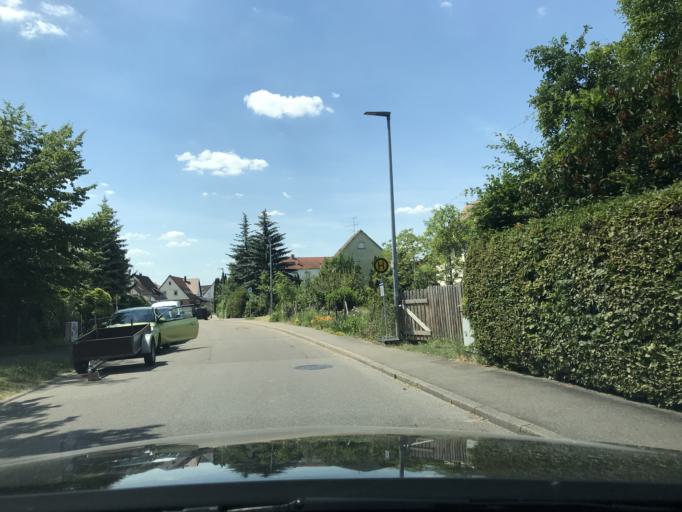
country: DE
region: Baden-Wuerttemberg
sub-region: Regierungsbezirk Stuttgart
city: Weinstadt-Endersbach
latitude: 48.8093
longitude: 9.3690
